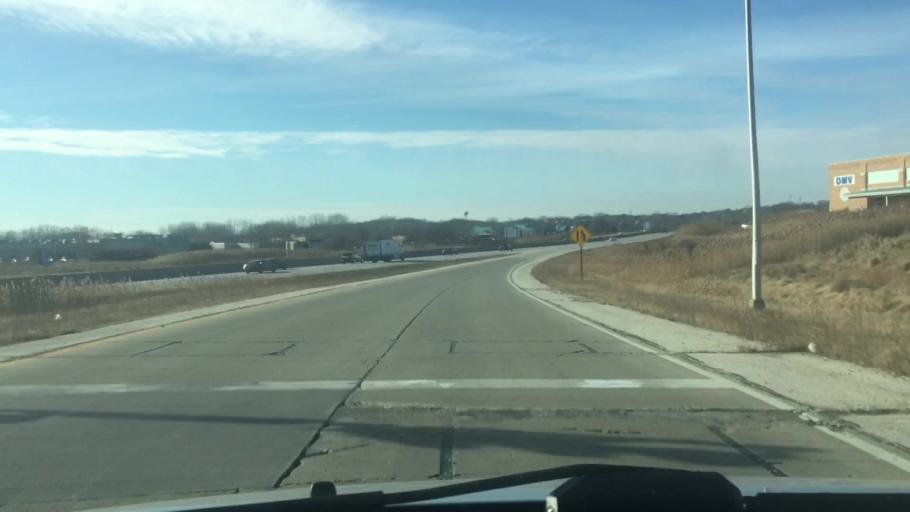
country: US
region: Wisconsin
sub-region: Waukesha County
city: Pewaukee
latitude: 43.0470
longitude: -88.2580
